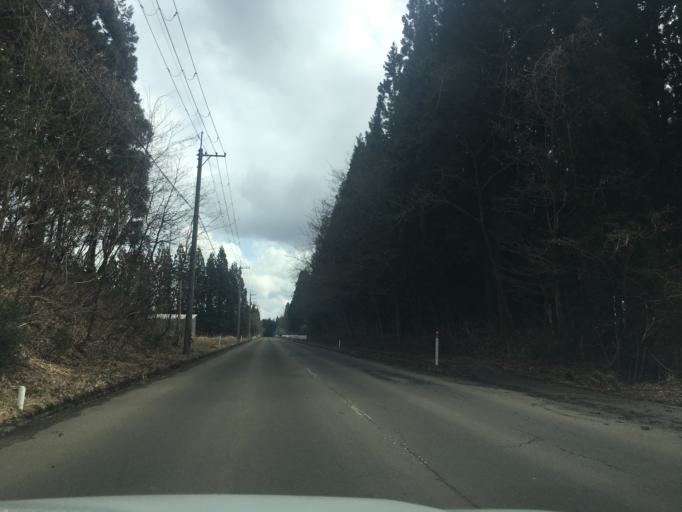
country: JP
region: Akita
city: Takanosu
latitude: 40.1890
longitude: 140.3462
